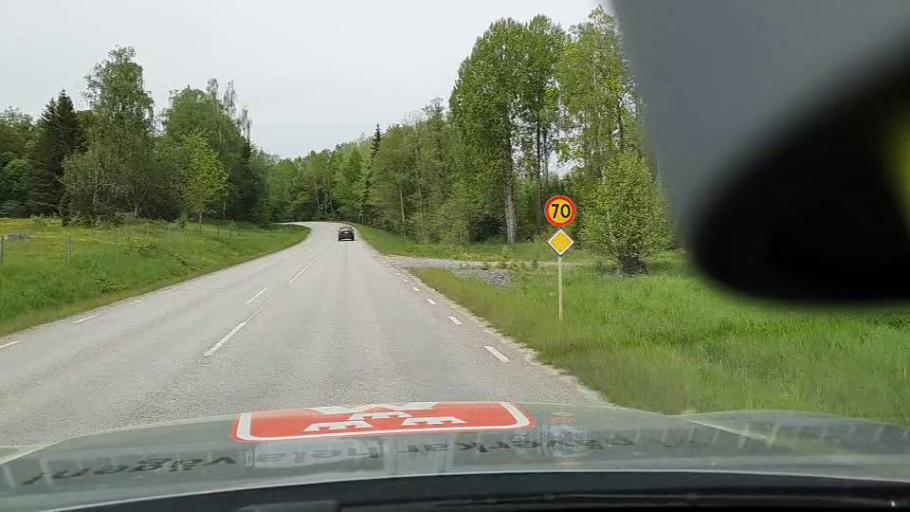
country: SE
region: Soedermanland
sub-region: Flens Kommun
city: Flen
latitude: 59.0869
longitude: 16.5854
